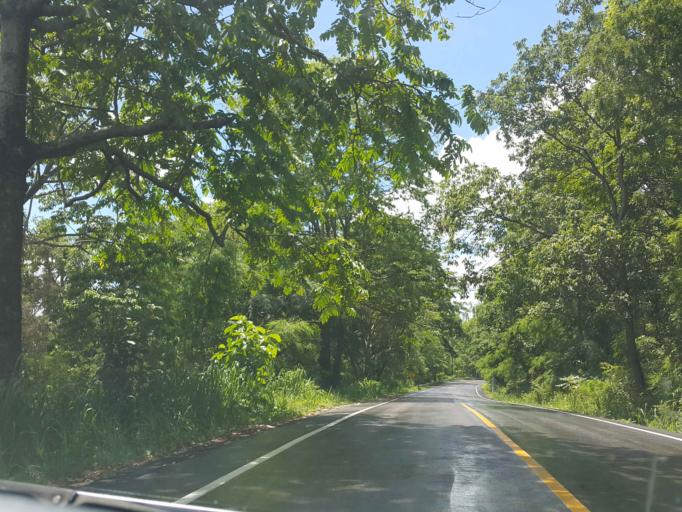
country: TH
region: Chiang Mai
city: Samoeng
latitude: 18.8518
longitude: 98.7720
